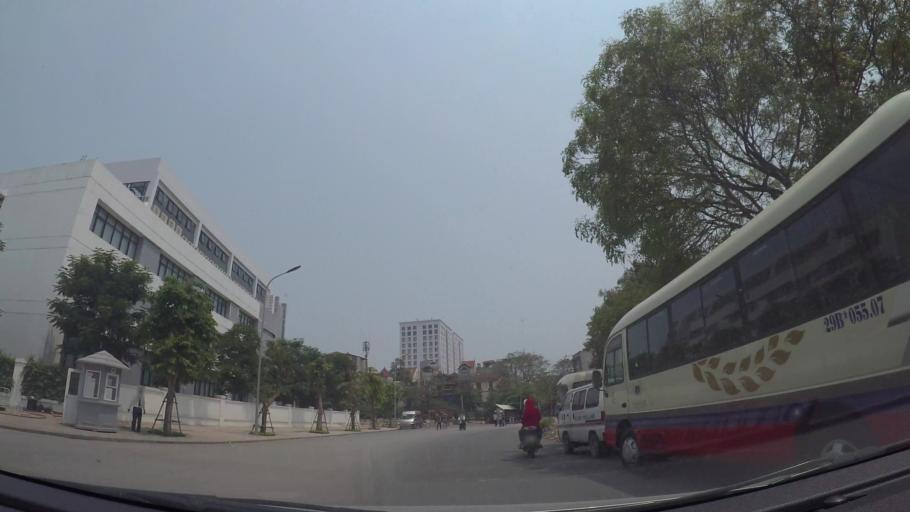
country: VN
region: Ha Noi
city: Thanh Xuan
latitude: 20.9981
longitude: 105.7870
